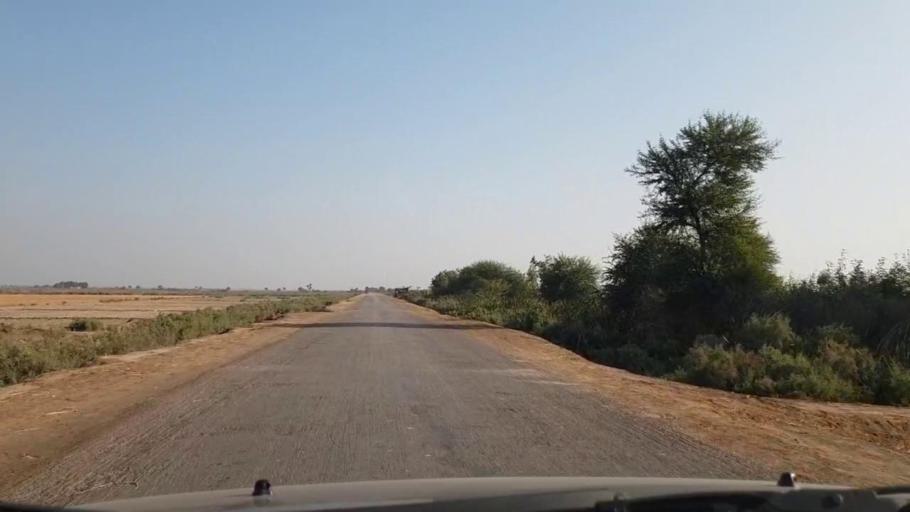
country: PK
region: Sindh
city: Tando Bago
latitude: 24.8259
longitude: 69.0119
